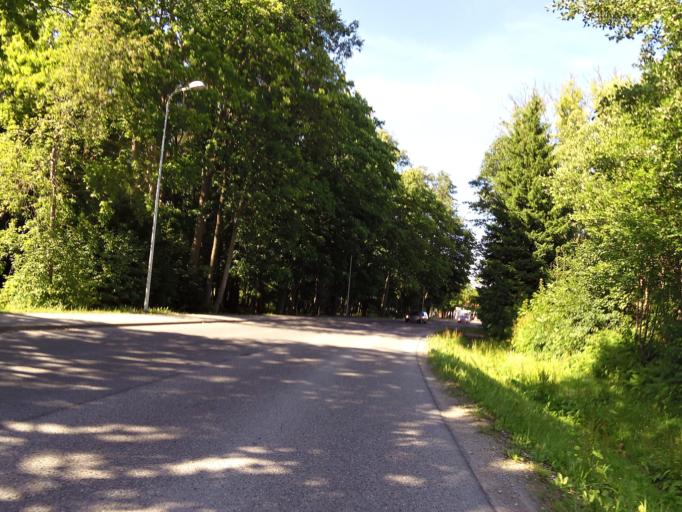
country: EE
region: Hiiumaa
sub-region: Kaerdla linn
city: Kardla
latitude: 58.9957
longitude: 22.7461
